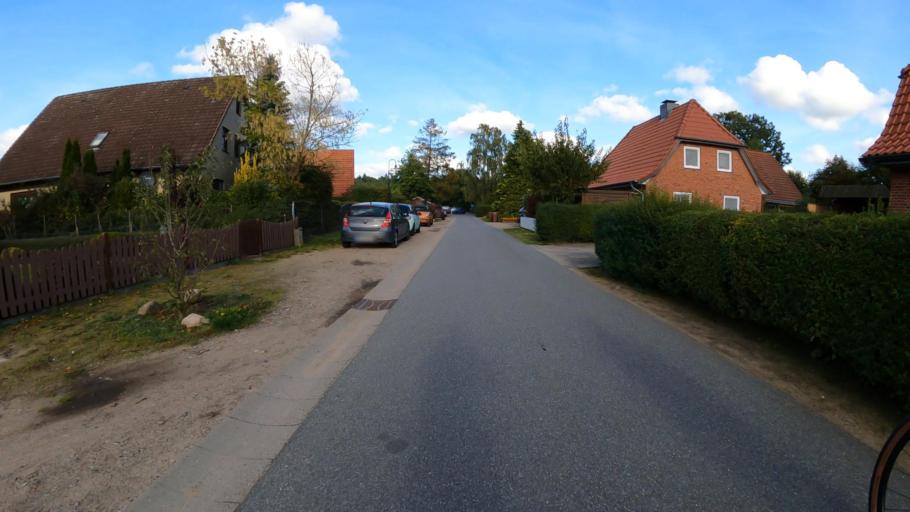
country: DE
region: Schleswig-Holstein
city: Hartenholm
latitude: 53.9013
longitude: 10.0630
